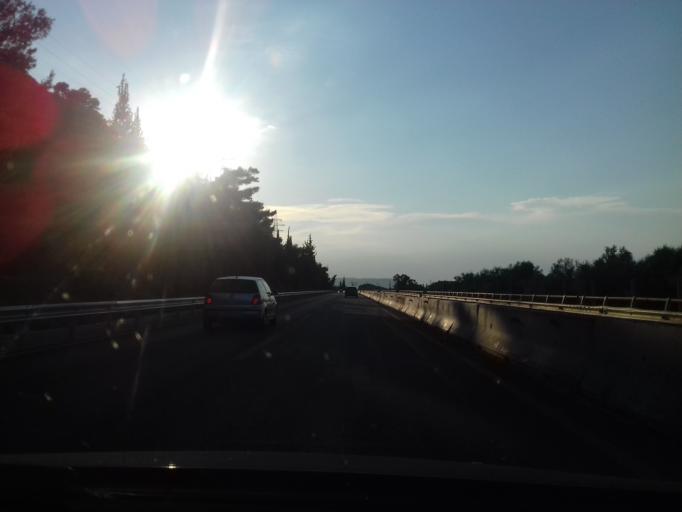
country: GR
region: West Greece
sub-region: Nomos Achaias
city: Aiyira
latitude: 38.1328
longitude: 22.4364
